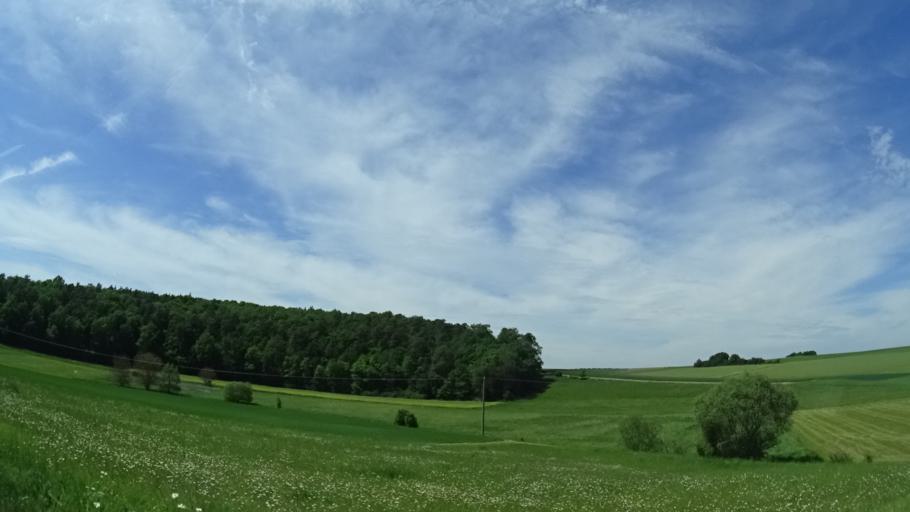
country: DE
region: Bavaria
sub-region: Regierungsbezirk Unterfranken
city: Arnstein
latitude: 50.0017
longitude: 9.9863
